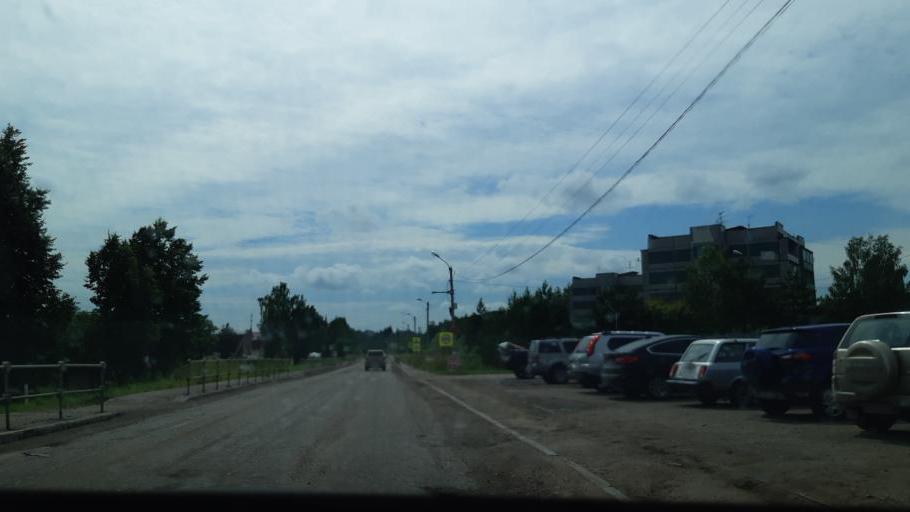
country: RU
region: Moskovskaya
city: Vereya
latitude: 55.3362
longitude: 36.1611
